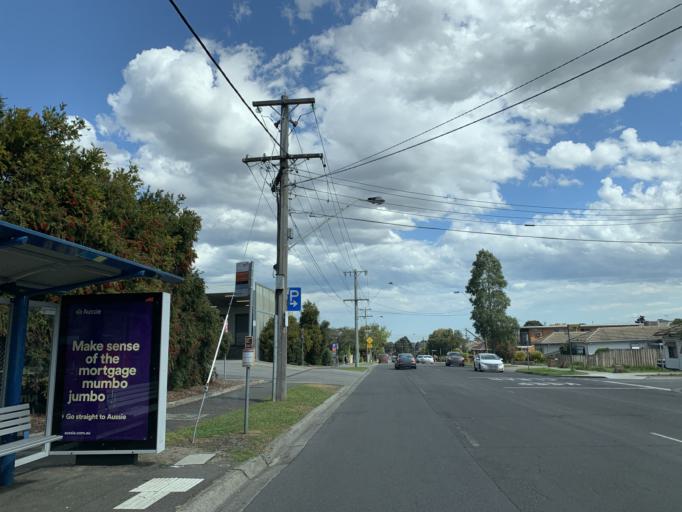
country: AU
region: Victoria
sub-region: Moonee Valley
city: Niddrie
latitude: -37.7377
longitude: 144.8924
